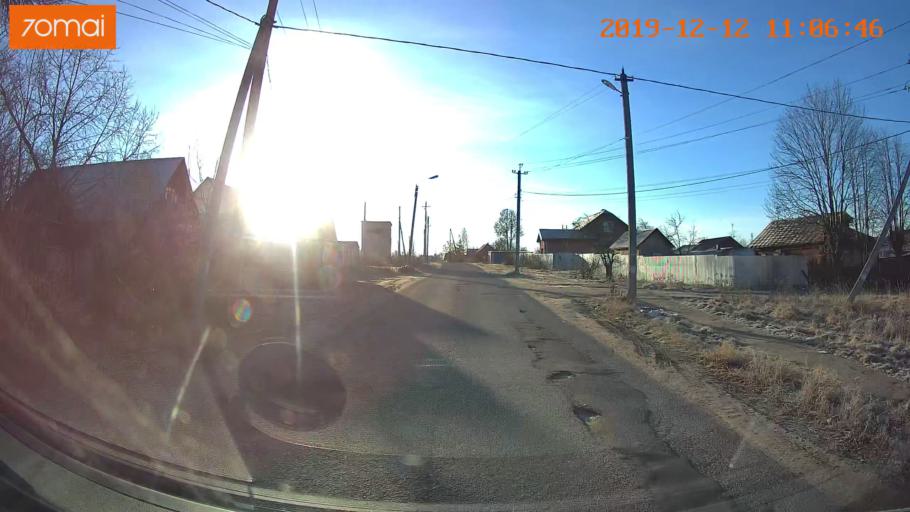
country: RU
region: Ivanovo
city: Kokhma
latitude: 56.9417
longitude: 41.0885
